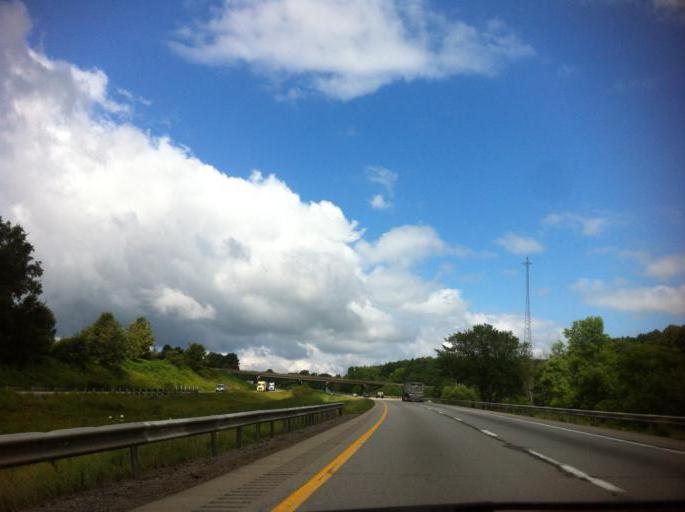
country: US
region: Pennsylvania
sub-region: Lawrence County
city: New Wilmington
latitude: 41.1841
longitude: -80.3233
